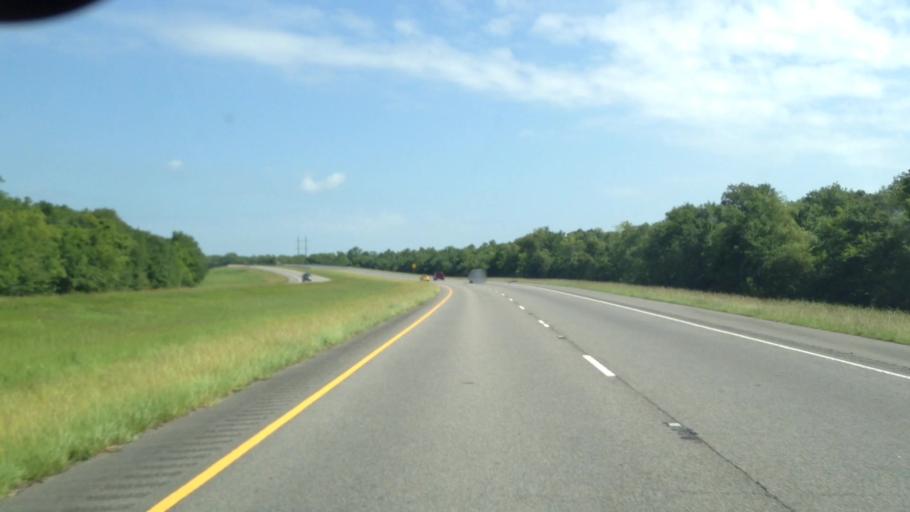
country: US
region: Louisiana
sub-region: Avoyelles Parish
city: Bunkie
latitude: 30.8930
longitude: -92.2268
